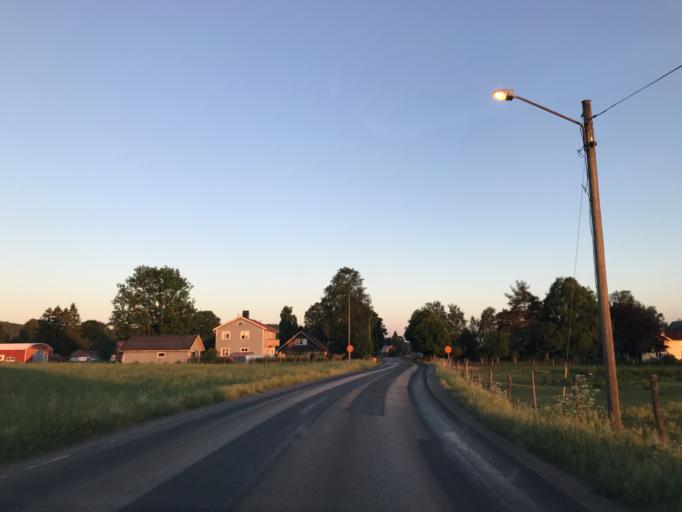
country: SE
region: Vaestra Goetaland
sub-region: Marks Kommun
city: Horred
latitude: 57.4289
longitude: 12.5200
